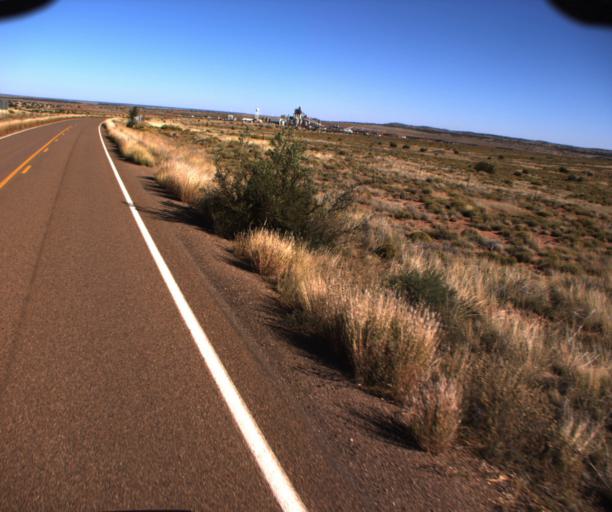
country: US
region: Arizona
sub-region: Navajo County
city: Heber-Overgaard
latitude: 34.4864
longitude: -110.3407
